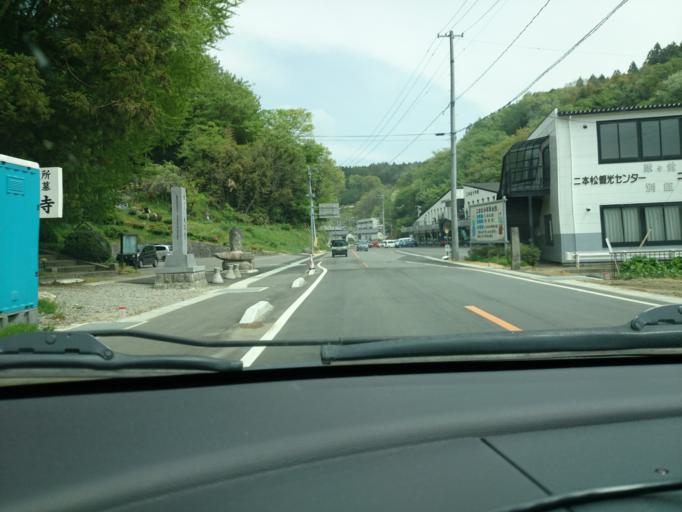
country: JP
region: Fukushima
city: Nihommatsu
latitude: 37.5919
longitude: 140.4243
